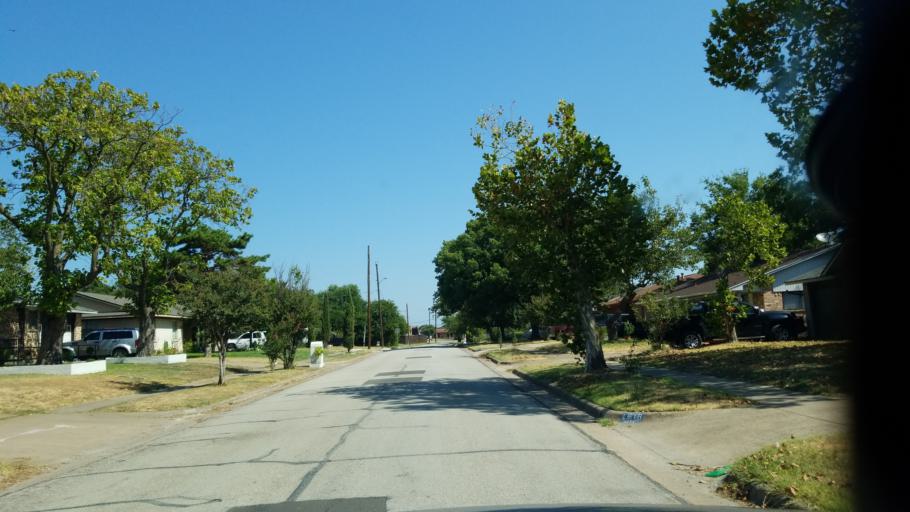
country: US
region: Texas
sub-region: Dallas County
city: Duncanville
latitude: 32.6439
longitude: -96.9010
